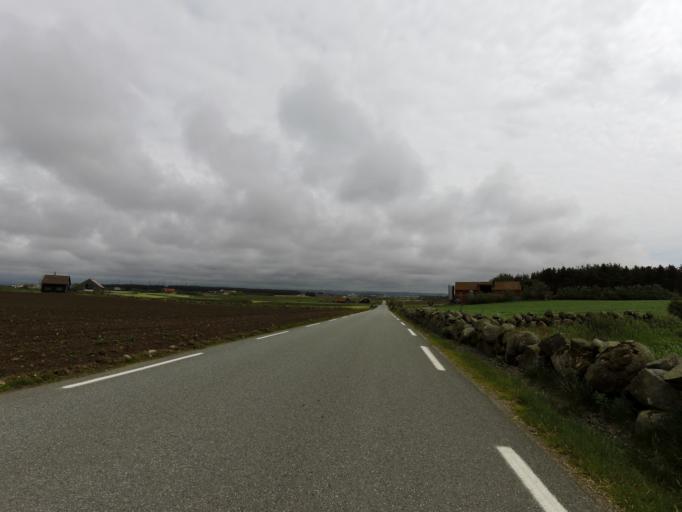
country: NO
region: Rogaland
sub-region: Ha
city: Naerbo
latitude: 58.6551
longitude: 5.5751
